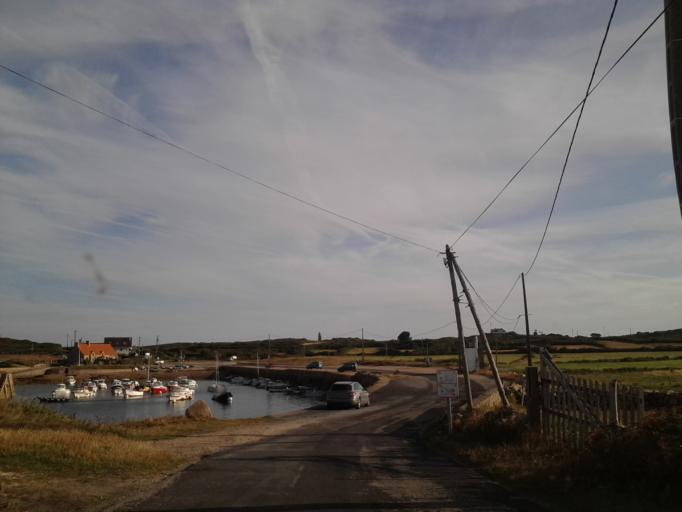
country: FR
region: Lower Normandy
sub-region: Departement de la Manche
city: Fermanville
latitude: 49.6861
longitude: -1.4725
